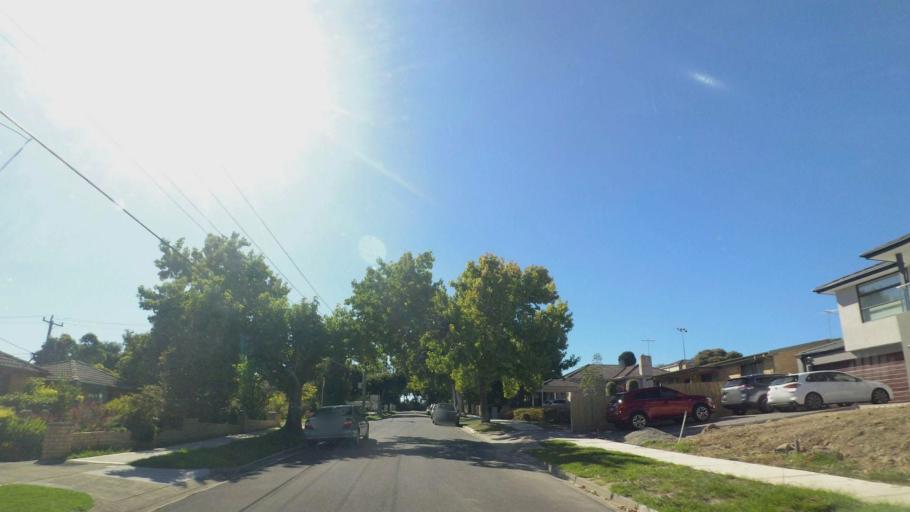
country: AU
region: Victoria
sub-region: Manningham
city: Donvale
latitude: -37.7962
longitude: 145.1740
